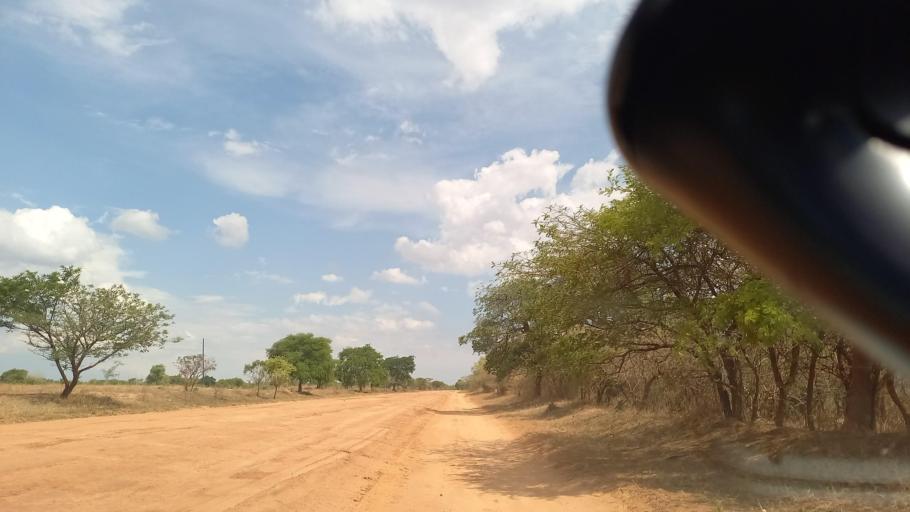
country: ZM
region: Lusaka
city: Kafue
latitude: -16.1166
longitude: 28.0342
